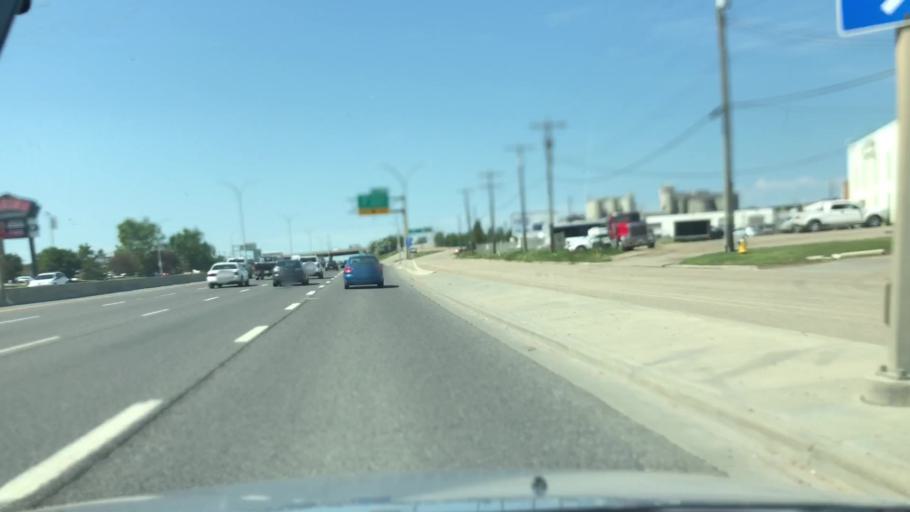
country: CA
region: Alberta
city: St. Albert
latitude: 53.5809
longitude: -113.5841
